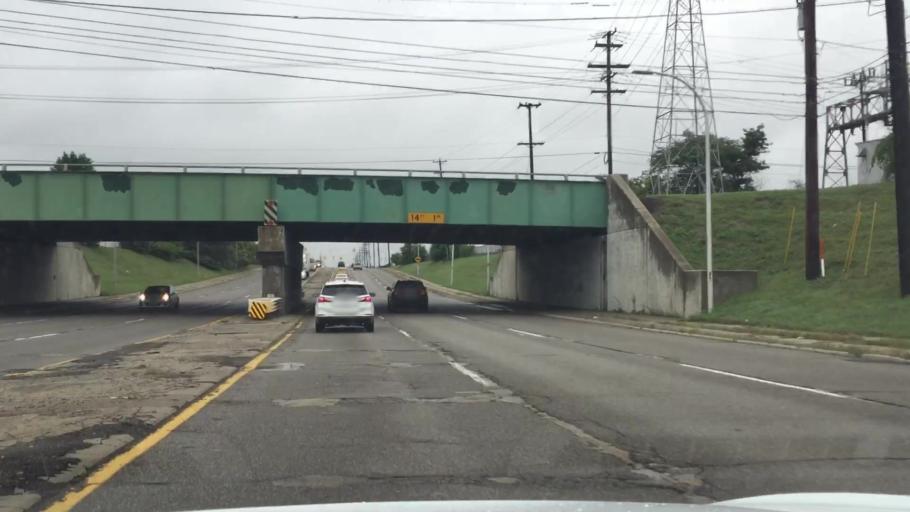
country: US
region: Michigan
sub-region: Wayne County
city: Livonia
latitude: 42.3769
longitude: -83.3335
